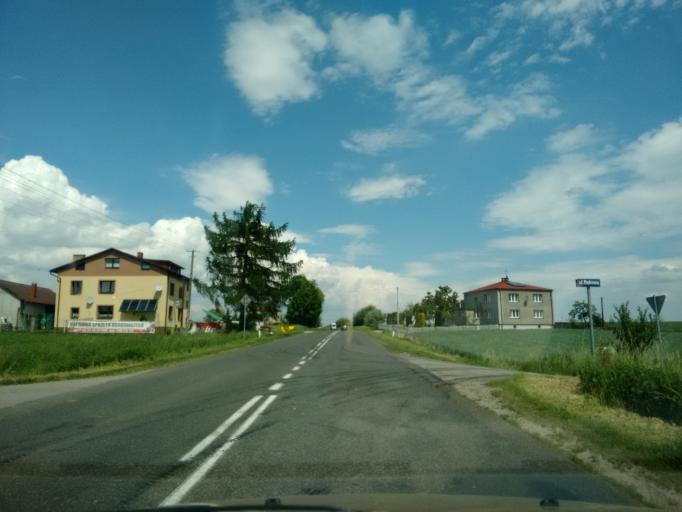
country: PL
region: Silesian Voivodeship
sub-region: Powiat cieszynski
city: Pruchna
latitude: 49.8578
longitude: 18.6765
